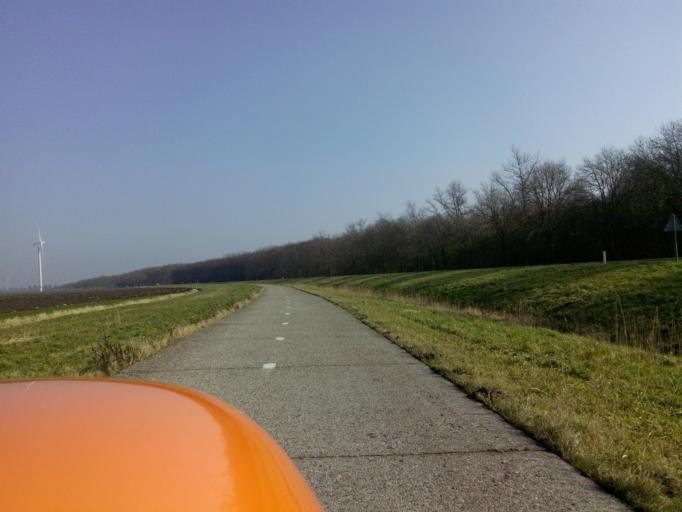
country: NL
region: Utrecht
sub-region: Gemeente Bunschoten
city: Bunschoten
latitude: 52.2669
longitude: 5.3904
